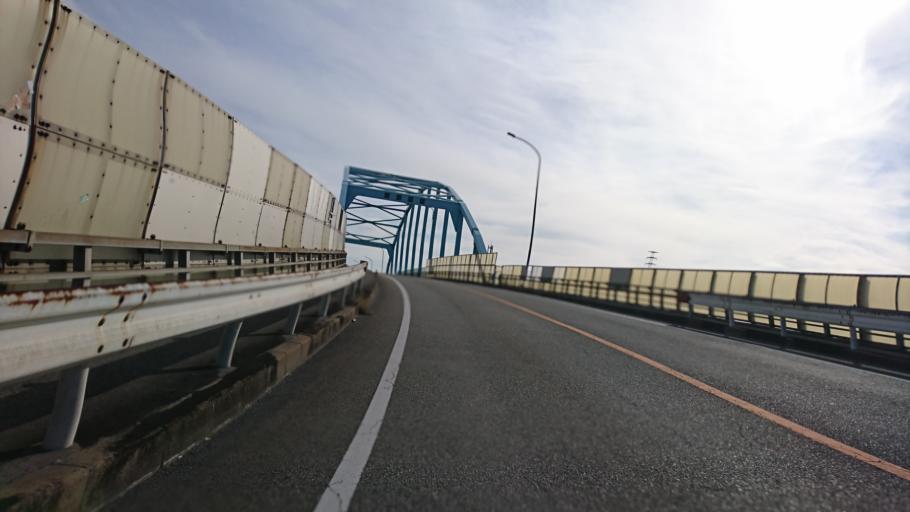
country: JP
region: Hyogo
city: Kakogawacho-honmachi
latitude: 34.7405
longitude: 134.8030
